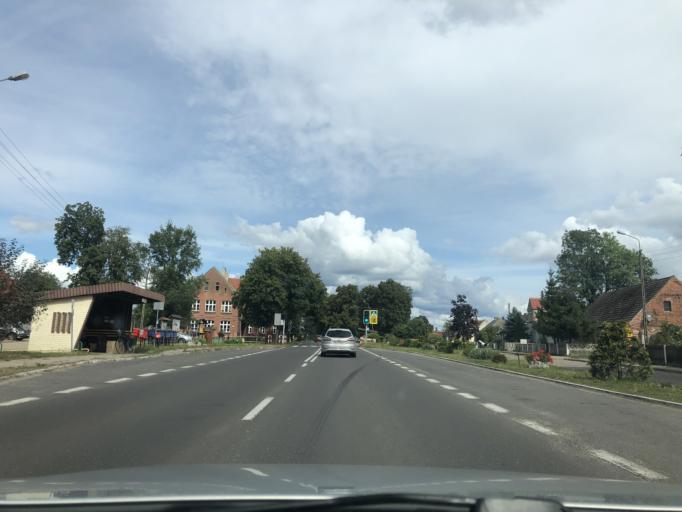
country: PL
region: Greater Poland Voivodeship
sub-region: Powiat pilski
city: Szydlowo
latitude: 53.0907
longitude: 16.6306
